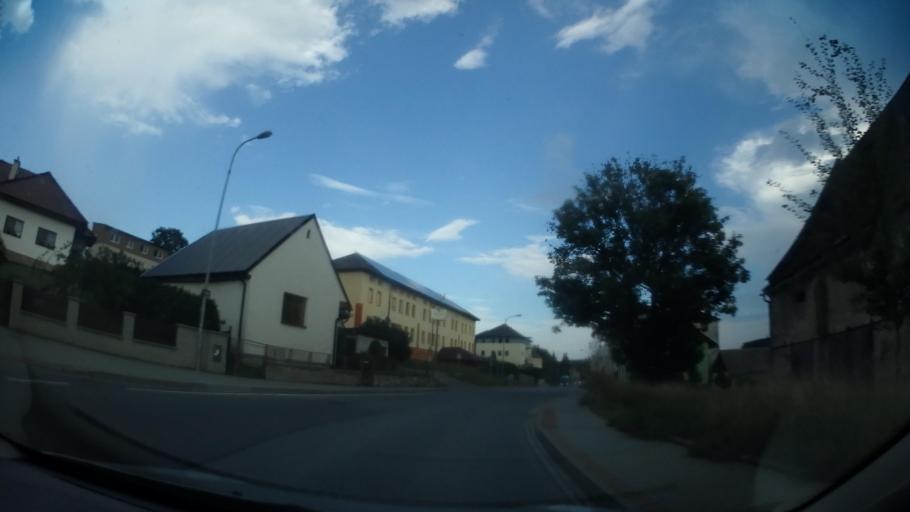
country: CZ
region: Olomoucky
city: Zabreh
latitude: 49.8867
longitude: 16.8648
